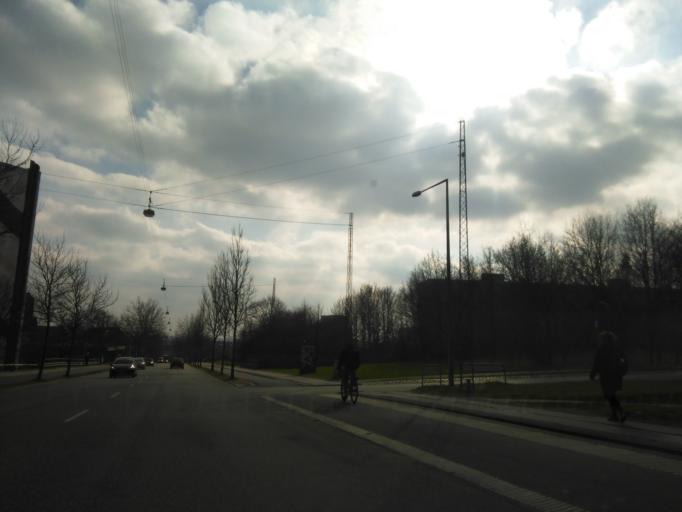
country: DK
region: Central Jutland
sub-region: Arhus Kommune
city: Arhus
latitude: 56.1634
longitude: 10.1969
